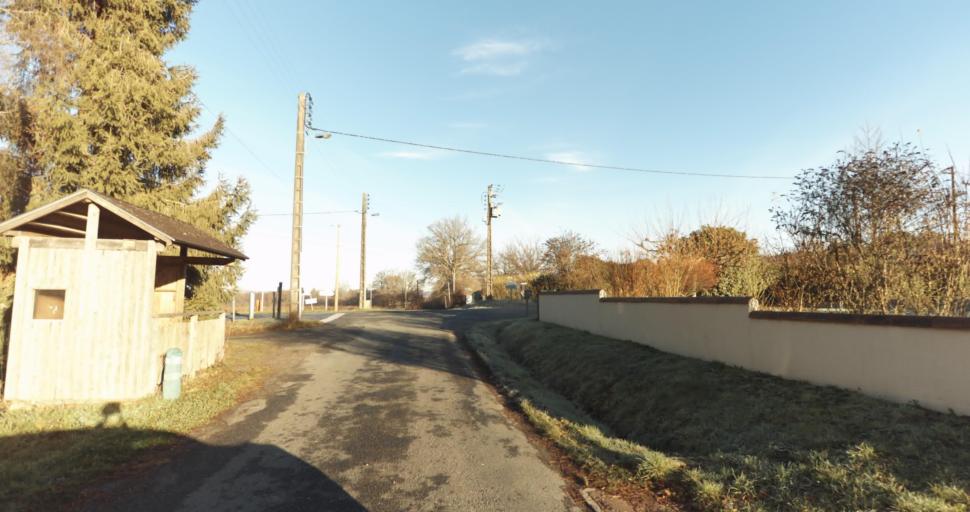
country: FR
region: Limousin
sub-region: Departement de la Haute-Vienne
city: Aixe-sur-Vienne
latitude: 45.8154
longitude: 1.1425
